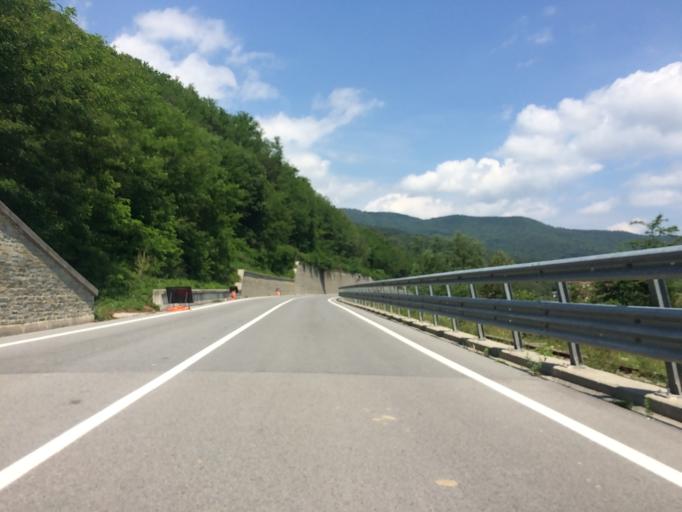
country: IT
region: Piedmont
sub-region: Provincia di Cuneo
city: Priola
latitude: 44.2517
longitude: 8.0212
